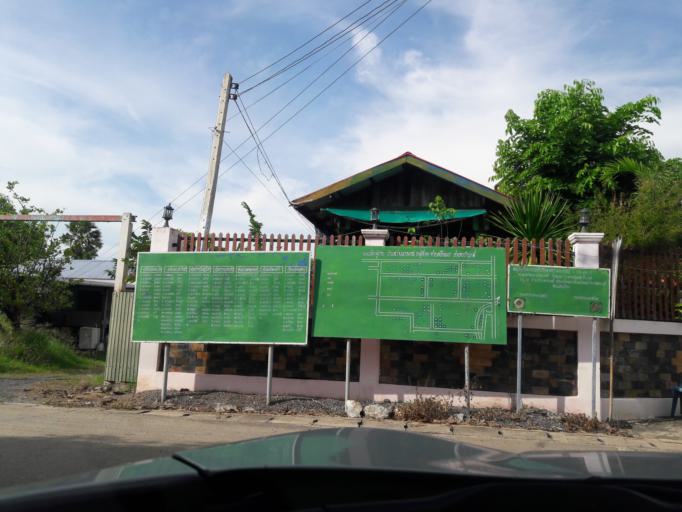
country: TH
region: Lop Buri
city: Ban Mi
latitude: 15.0457
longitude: 100.5317
